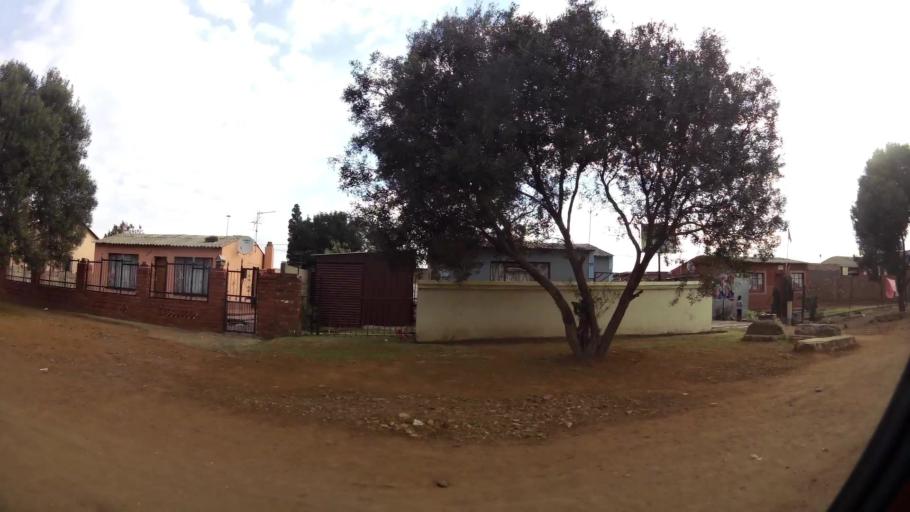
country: ZA
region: Gauteng
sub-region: Sedibeng District Municipality
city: Vanderbijlpark
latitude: -26.6818
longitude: 27.8770
